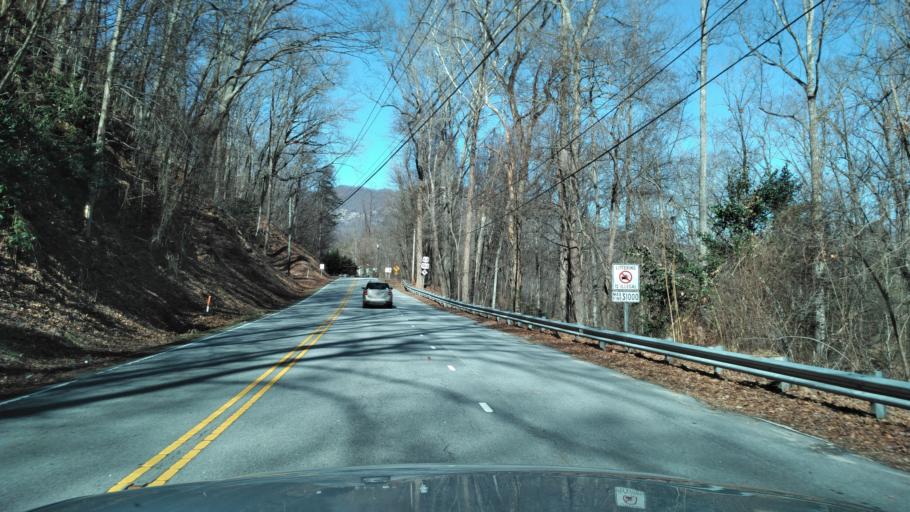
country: US
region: North Carolina
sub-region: Rutherford County
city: Lake Lure
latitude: 35.4250
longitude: -82.2017
